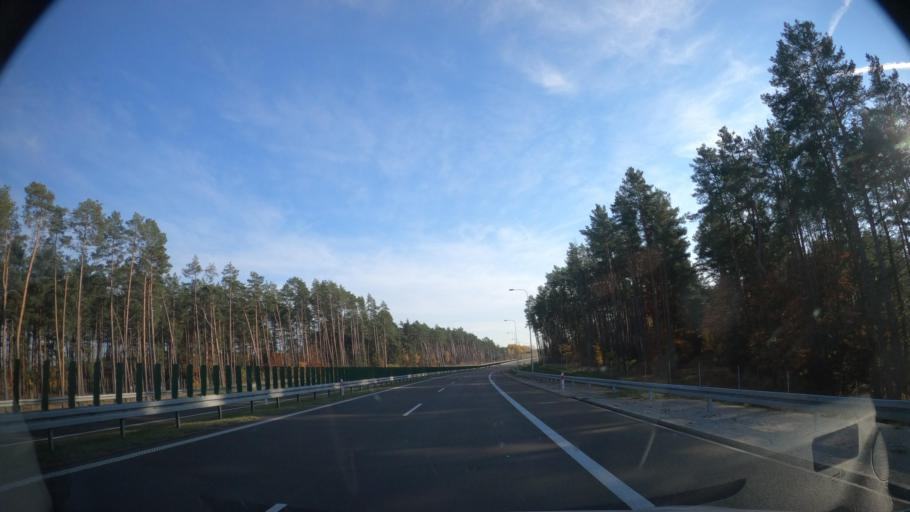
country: PL
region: West Pomeranian Voivodeship
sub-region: Powiat walecki
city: Walcz
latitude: 53.2913
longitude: 16.5015
